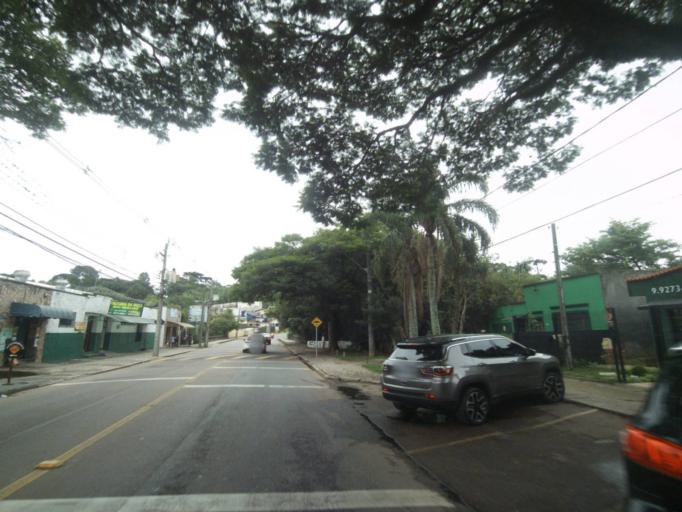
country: BR
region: Parana
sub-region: Curitiba
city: Curitiba
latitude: -25.4503
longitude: -49.3144
